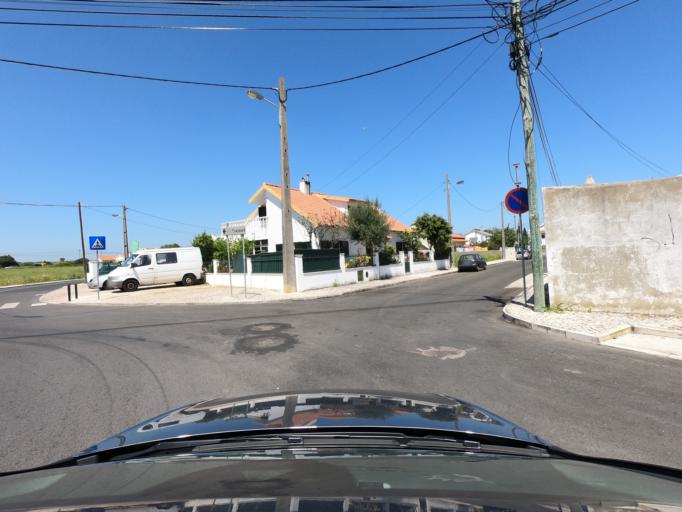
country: PT
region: Lisbon
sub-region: Cascais
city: Sao Domingos de Rana
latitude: 38.7288
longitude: -9.3411
